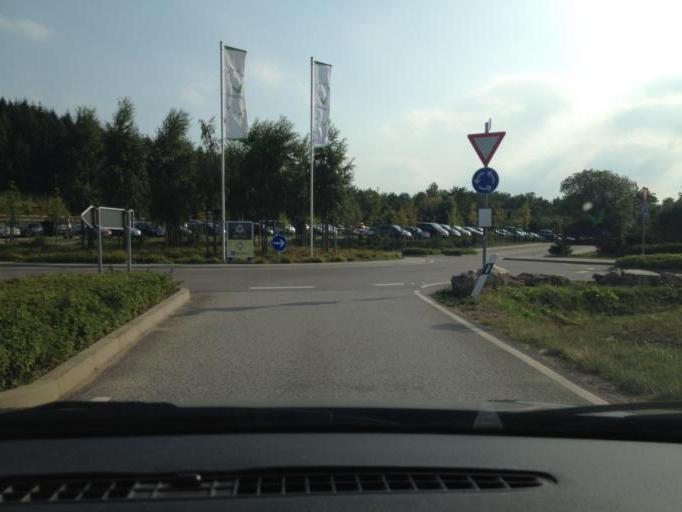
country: DE
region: Rheinland-Pfalz
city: Achtelsbach
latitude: 49.5705
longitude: 7.0856
